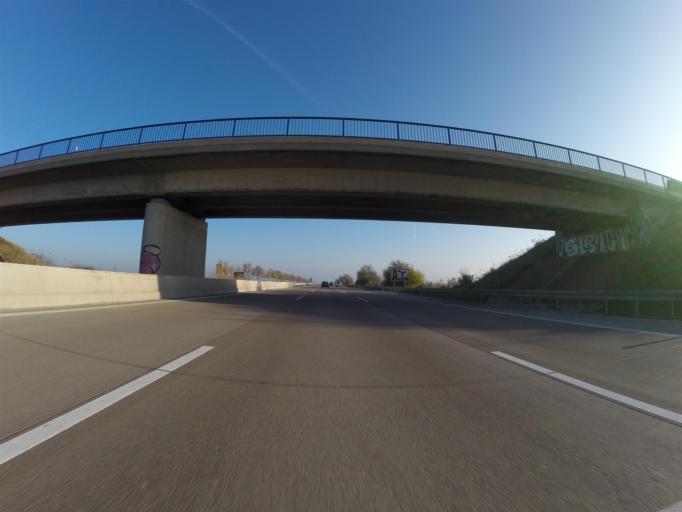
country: DE
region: Saxony-Anhalt
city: Tollwitz
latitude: 51.2604
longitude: 12.0893
